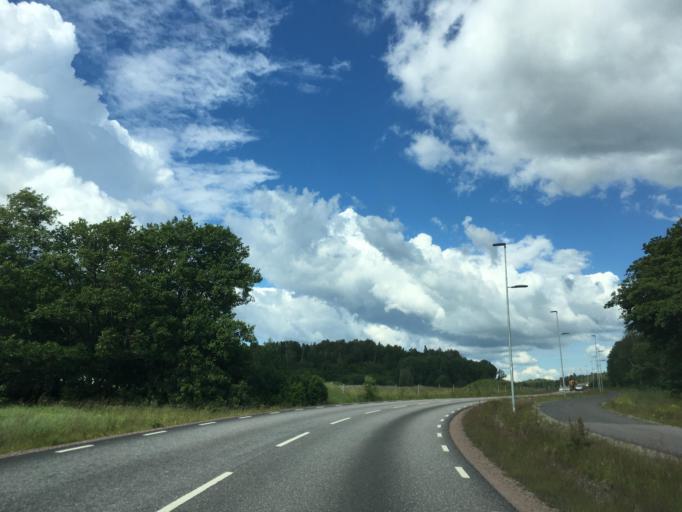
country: SE
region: Vaestra Goetaland
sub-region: Kungalvs Kommun
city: Kode
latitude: 57.8557
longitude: 11.8831
